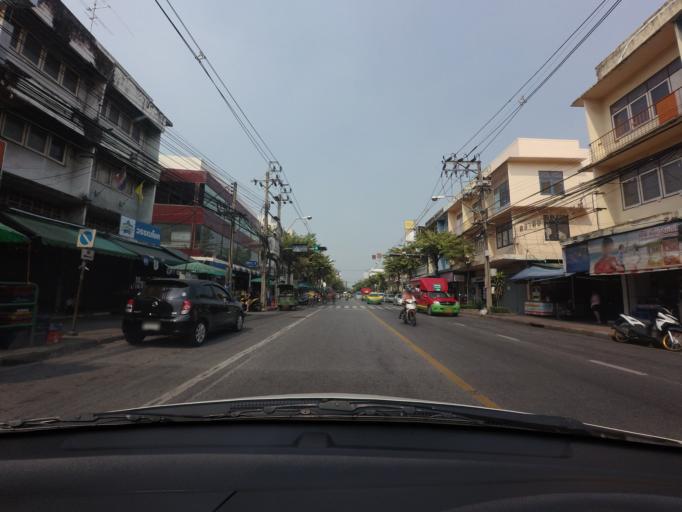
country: TH
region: Bangkok
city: Bangkok Noi
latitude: 13.7654
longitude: 100.4726
